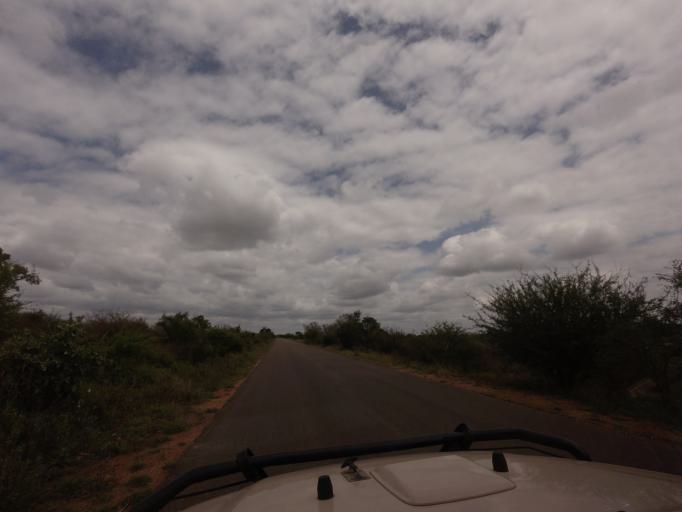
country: ZA
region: Mpumalanga
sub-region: Ehlanzeni District
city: Komatipoort
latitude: -25.1022
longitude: 31.8936
